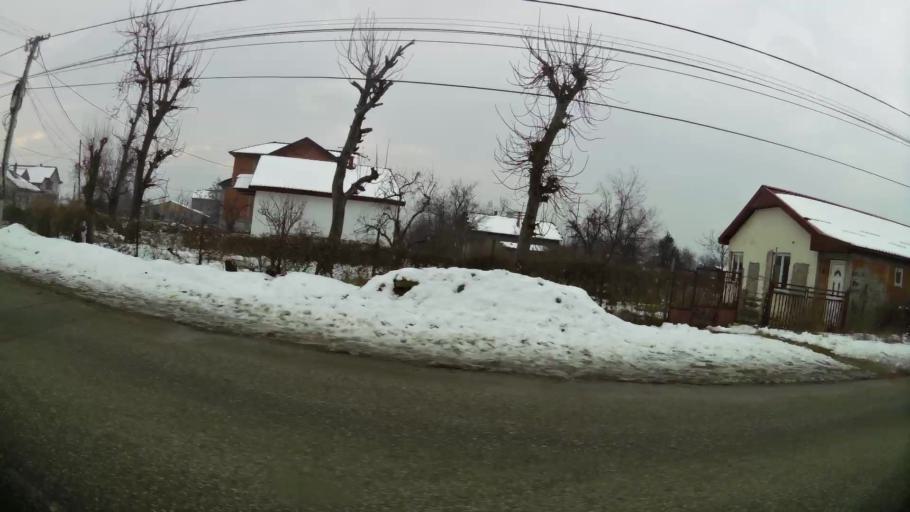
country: MK
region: Saraj
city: Saraj
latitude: 42.0438
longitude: 21.3559
